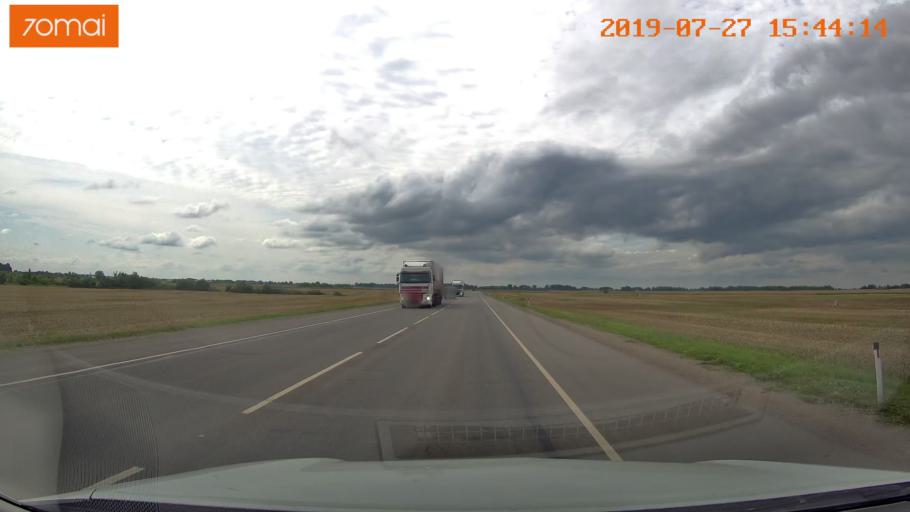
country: RU
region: Kaliningrad
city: Gusev
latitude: 54.6149
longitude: 22.1708
